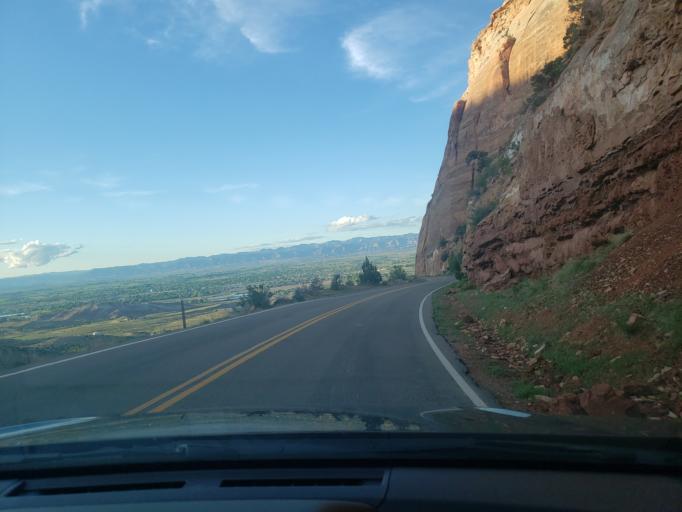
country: US
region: Colorado
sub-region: Mesa County
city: Fruita
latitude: 39.1127
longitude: -108.7315
